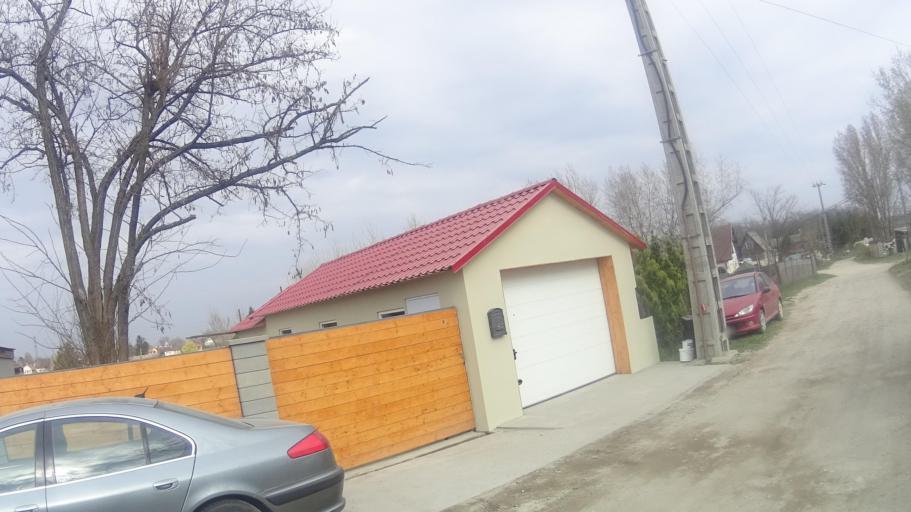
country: HU
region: Pest
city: Dunaharaszti
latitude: 47.3853
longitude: 19.0674
